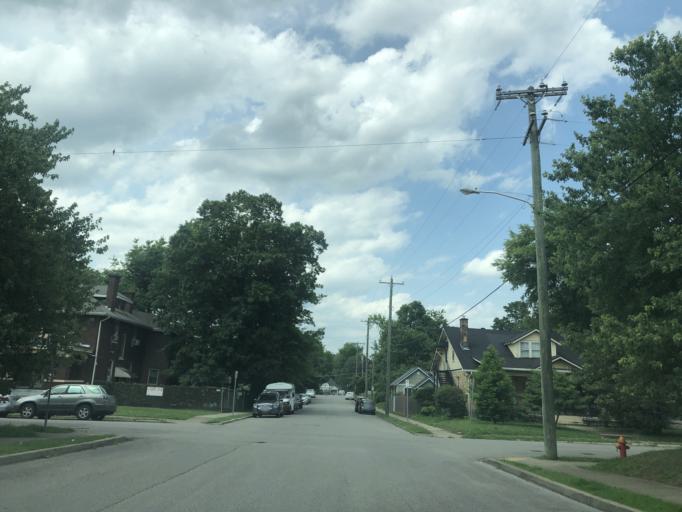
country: US
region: Tennessee
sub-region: Davidson County
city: Nashville
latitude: 36.1791
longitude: -86.7482
